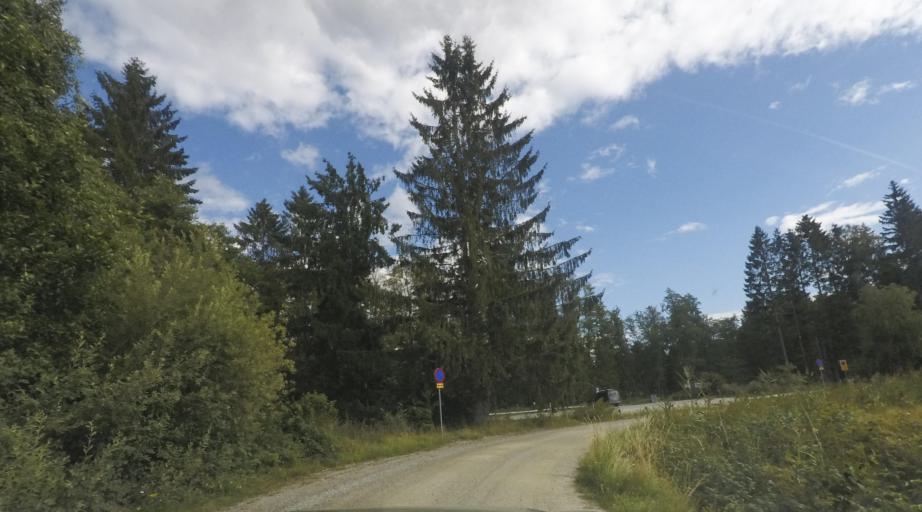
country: SE
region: Stockholm
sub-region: Sodertalje Kommun
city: Pershagen
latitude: 59.1065
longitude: 17.6785
